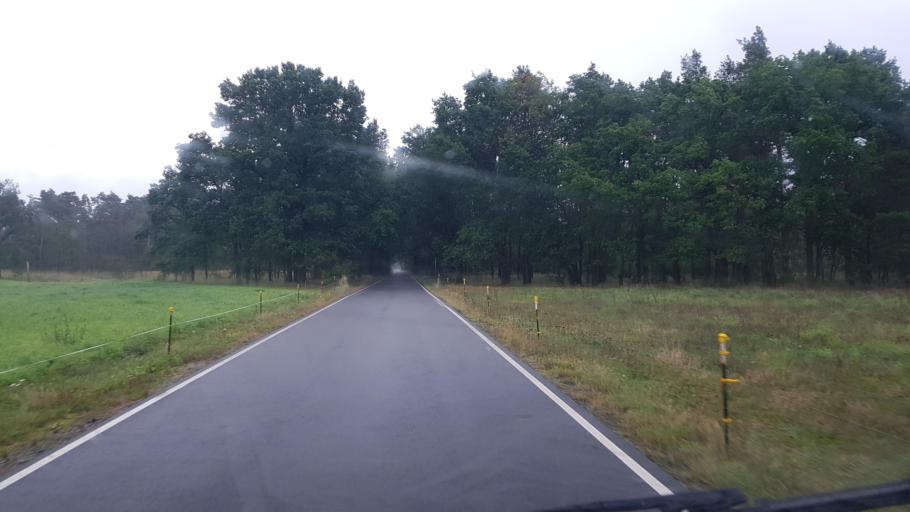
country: DE
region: Brandenburg
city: Lindenau
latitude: 51.4005
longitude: 13.7354
